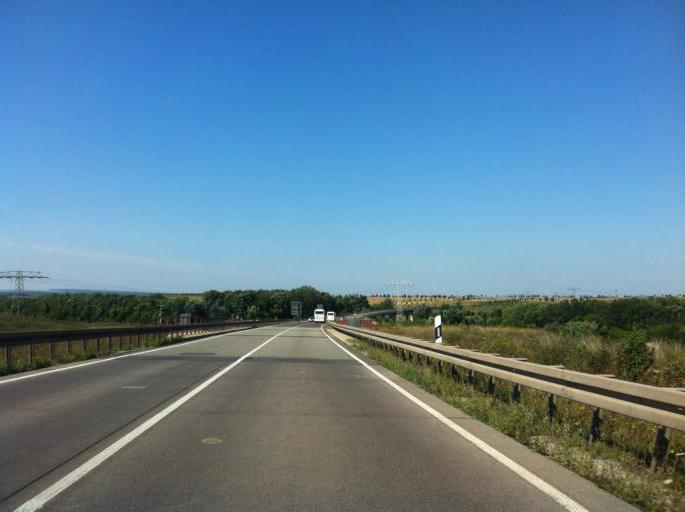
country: DE
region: Thuringia
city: Bad Langensalza
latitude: 51.0933
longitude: 10.6302
